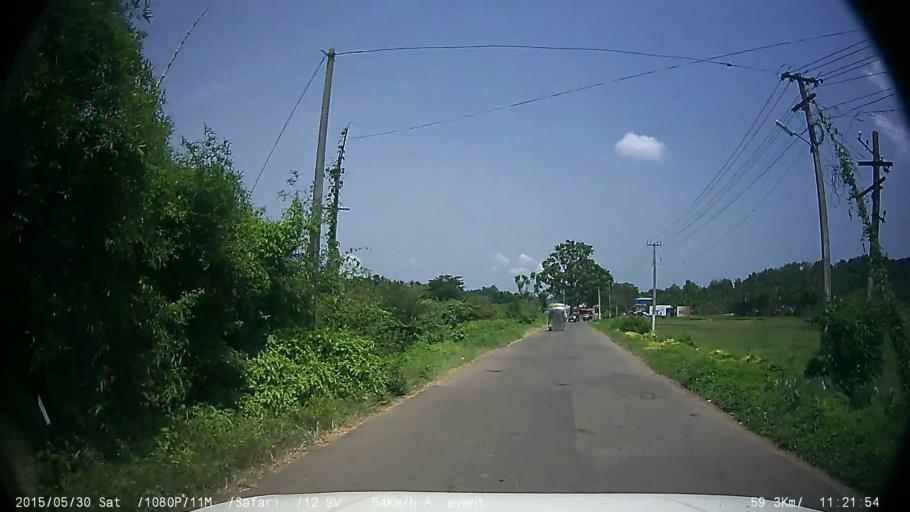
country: IN
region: Kerala
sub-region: Wayanad
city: Panamaram
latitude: 11.8025
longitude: 76.0342
